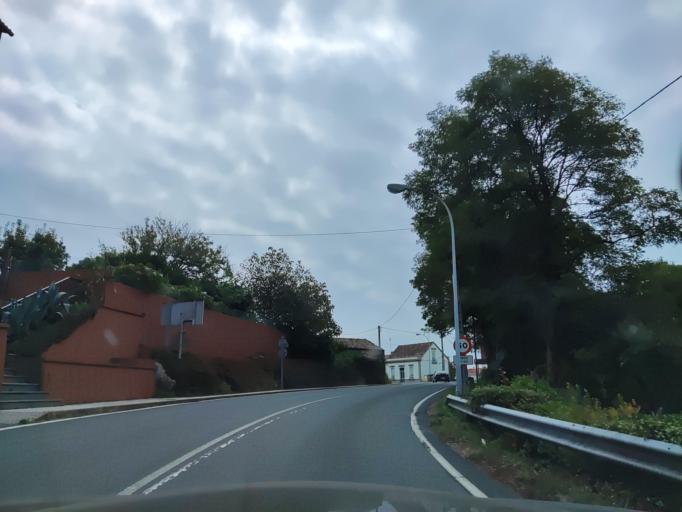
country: ES
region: Galicia
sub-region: Provincia da Coruna
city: Boiro
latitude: 42.6464
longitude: -8.8924
